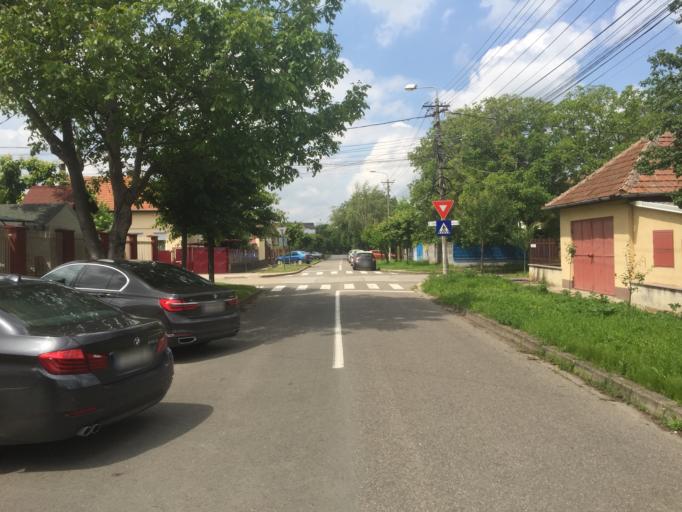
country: RO
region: Timis
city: Timisoara
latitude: 45.7566
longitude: 21.2014
